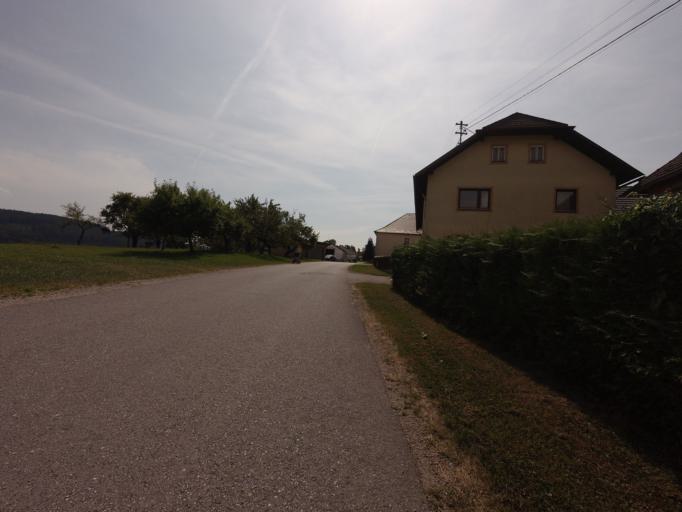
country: AT
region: Upper Austria
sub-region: Politischer Bezirk Urfahr-Umgebung
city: Reichenthal
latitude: 48.5299
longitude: 14.3616
